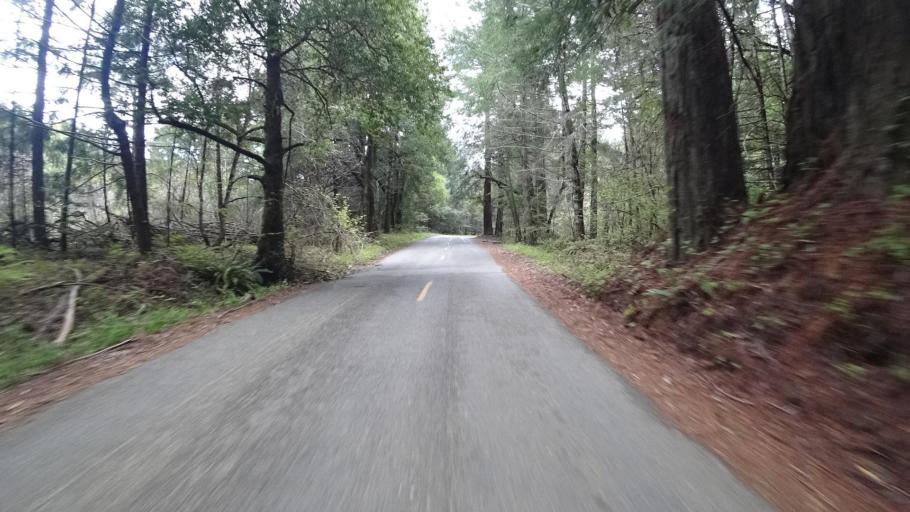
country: US
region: California
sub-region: Humboldt County
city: Redway
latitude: 40.0108
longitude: -123.9303
